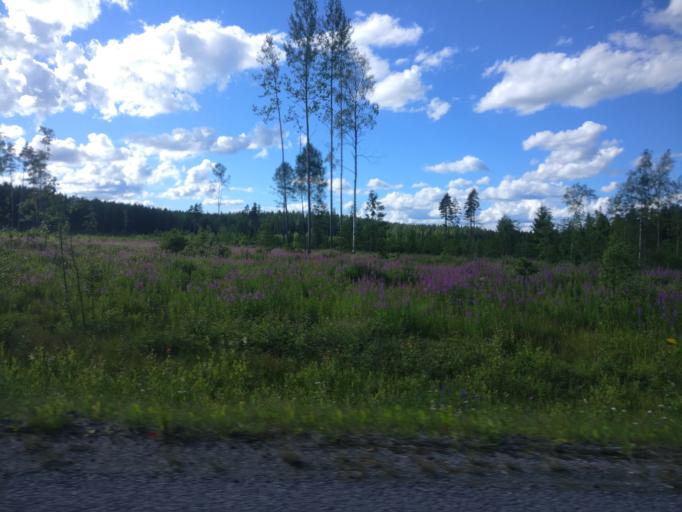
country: FI
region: Uusimaa
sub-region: Helsinki
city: Hyvinge
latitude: 60.5867
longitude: 24.8391
